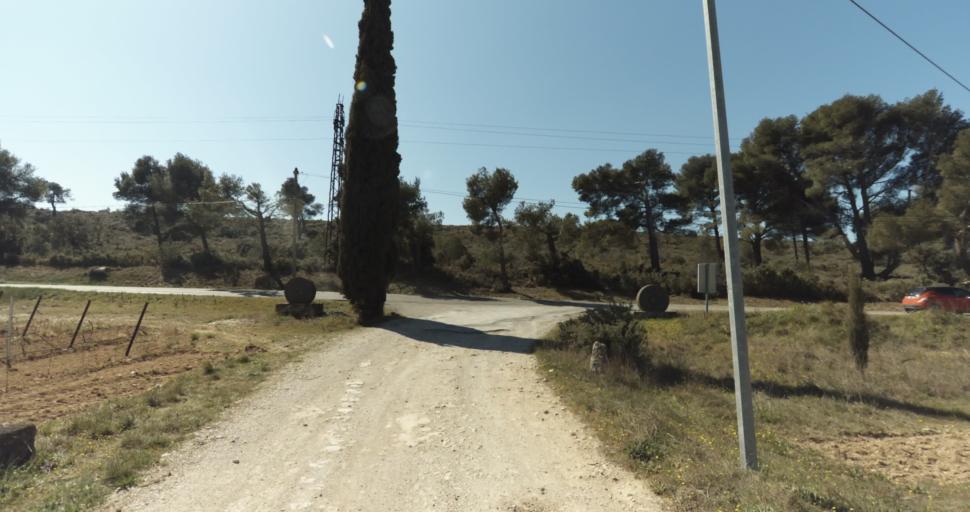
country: FR
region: Provence-Alpes-Cote d'Azur
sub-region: Departement des Bouches-du-Rhone
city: La Fare-les-Oliviers
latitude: 43.6027
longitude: 5.1925
